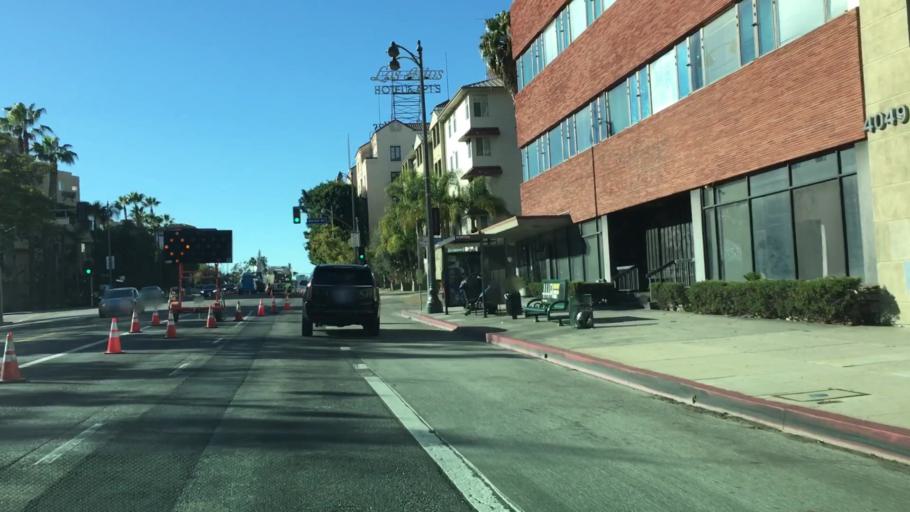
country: US
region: California
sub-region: Los Angeles County
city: Hollywood
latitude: 34.0618
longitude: -118.3161
